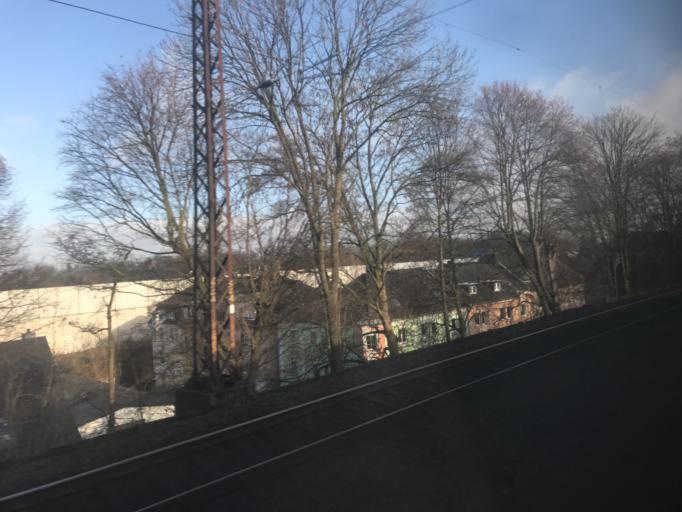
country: DE
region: North Rhine-Westphalia
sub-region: Regierungsbezirk Munster
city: Gelsenkirchen
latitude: 51.4735
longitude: 7.1437
